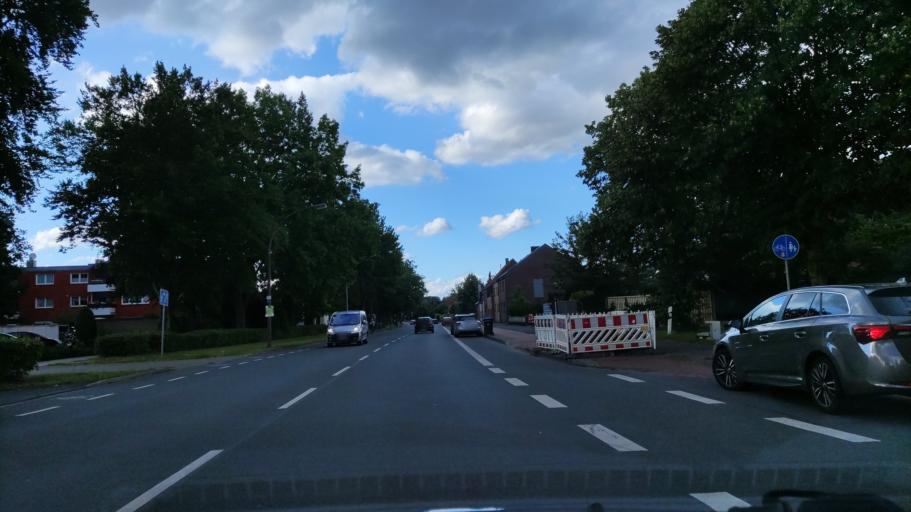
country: DE
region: North Rhine-Westphalia
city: Ahlen
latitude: 51.7502
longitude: 7.8978
